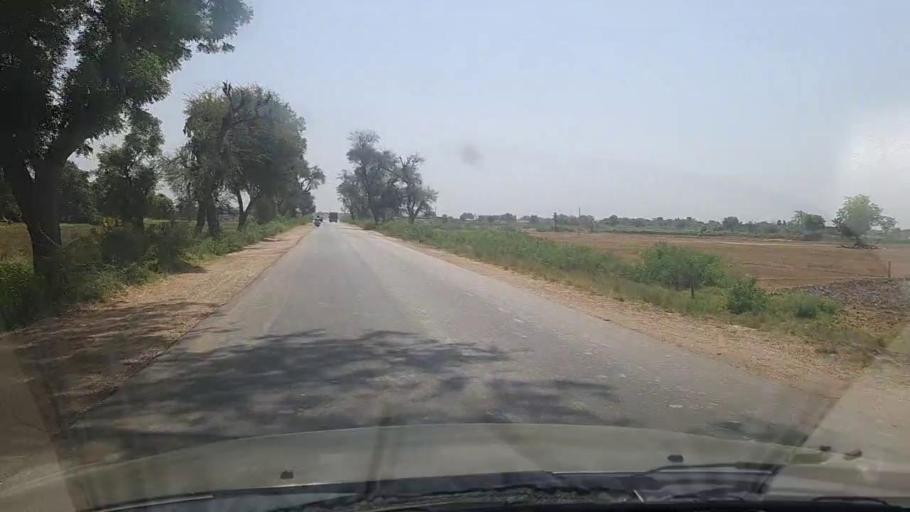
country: PK
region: Sindh
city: Tando Jam
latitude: 25.3655
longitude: 68.4846
